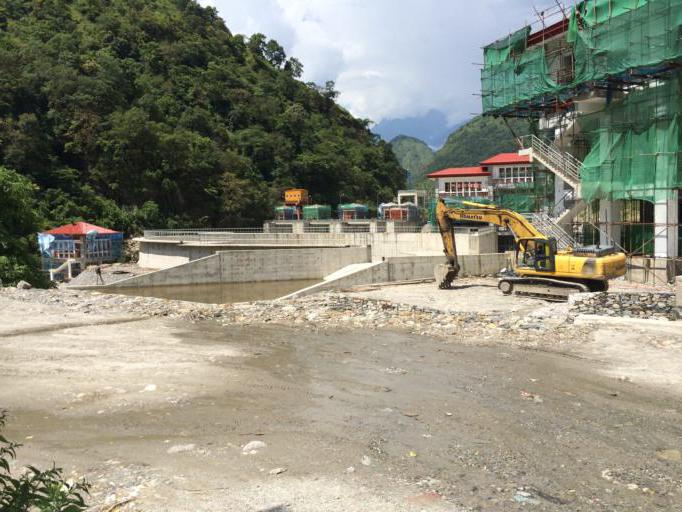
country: NP
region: Western Region
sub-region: Gandaki Zone
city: Khudi
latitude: 28.3100
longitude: 84.4003
